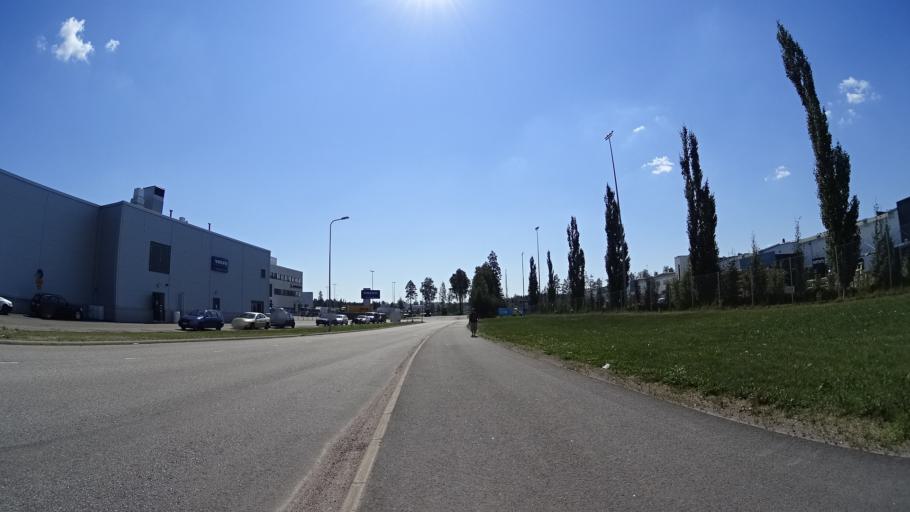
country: FI
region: Uusimaa
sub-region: Helsinki
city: Vantaa
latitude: 60.2999
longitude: 24.9326
